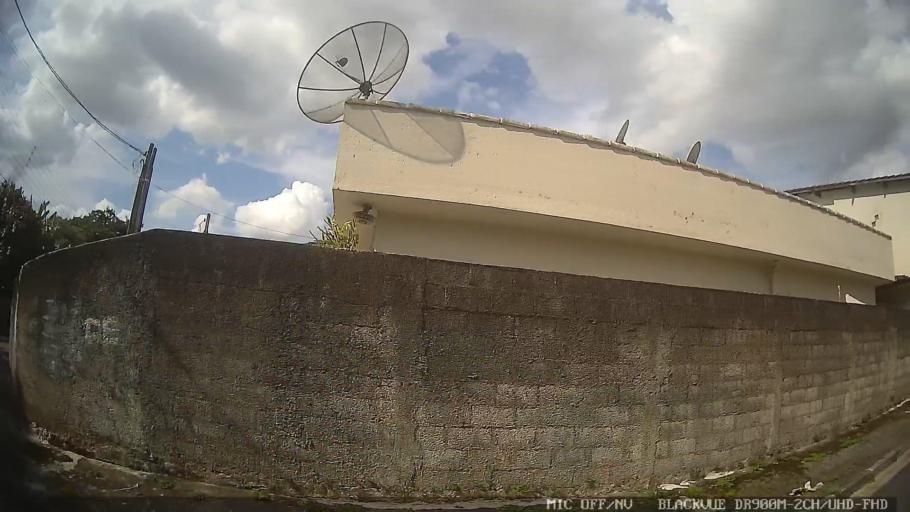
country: BR
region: Sao Paulo
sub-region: Atibaia
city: Atibaia
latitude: -23.1206
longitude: -46.5776
